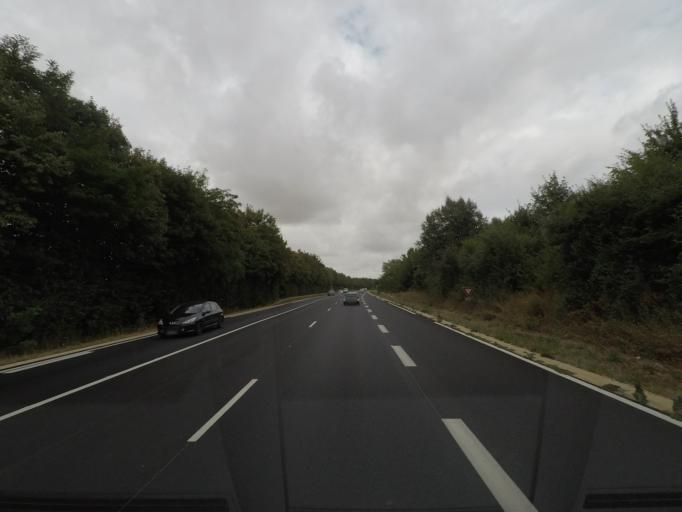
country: FR
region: Poitou-Charentes
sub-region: Departement des Deux-Sevres
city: Celles-sur-Belle
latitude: 46.2558
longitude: -0.2251
